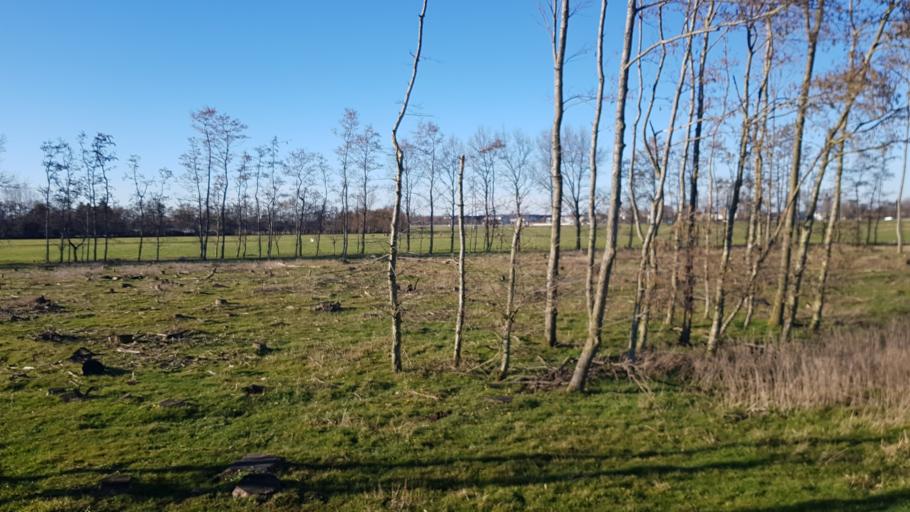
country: NL
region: South Holland
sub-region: Gemeente Leiderdorp
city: Leiderdorp
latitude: 52.1290
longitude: 4.5300
